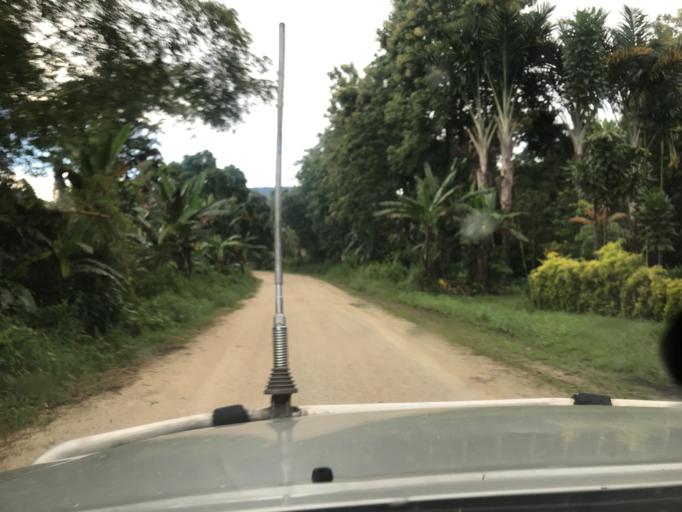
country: SB
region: Malaita
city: Auki
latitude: -8.5297
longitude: 160.7141
